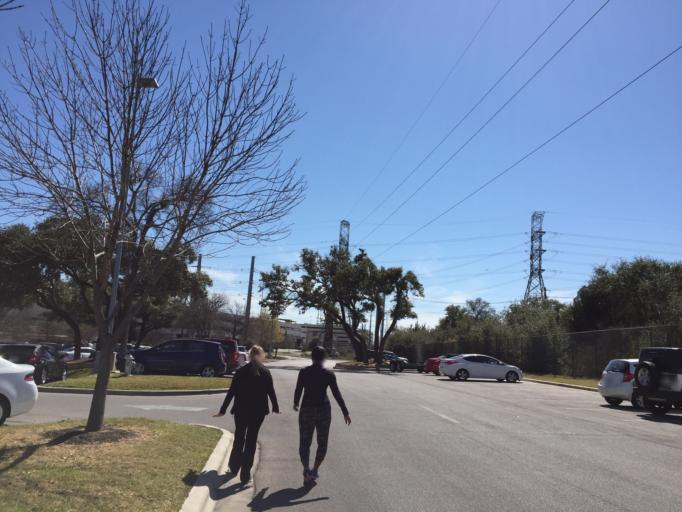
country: US
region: Texas
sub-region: Williamson County
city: Jollyville
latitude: 30.4002
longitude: -97.7280
